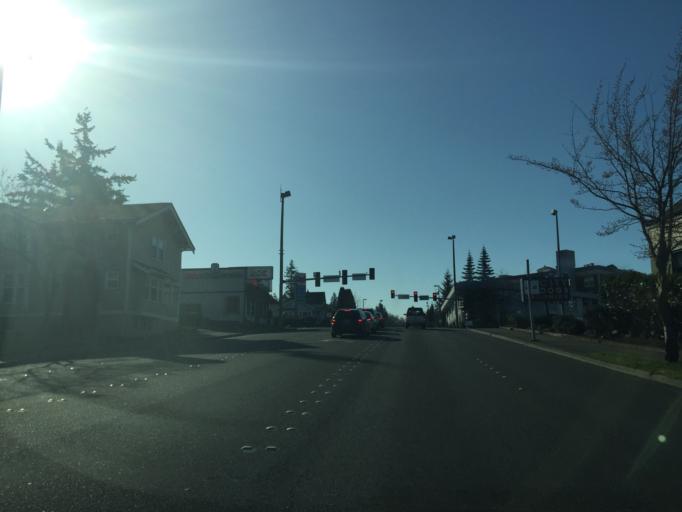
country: US
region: Washington
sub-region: Whatcom County
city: Bellingham
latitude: 48.7458
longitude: -122.4718
